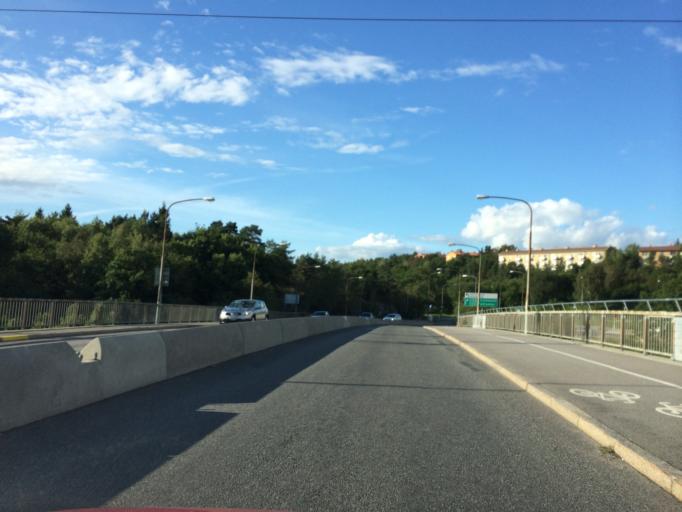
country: SE
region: Stockholm
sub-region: Huddinge Kommun
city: Huddinge
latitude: 59.2890
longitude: 17.9813
